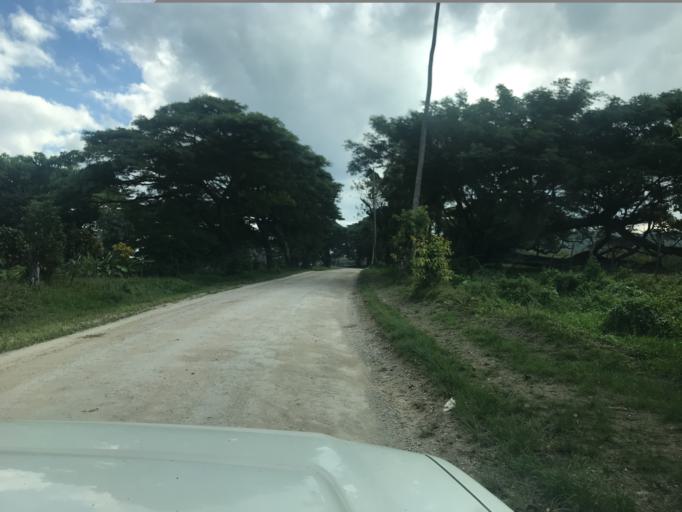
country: VU
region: Sanma
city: Luganville
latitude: -15.5790
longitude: 167.1211
